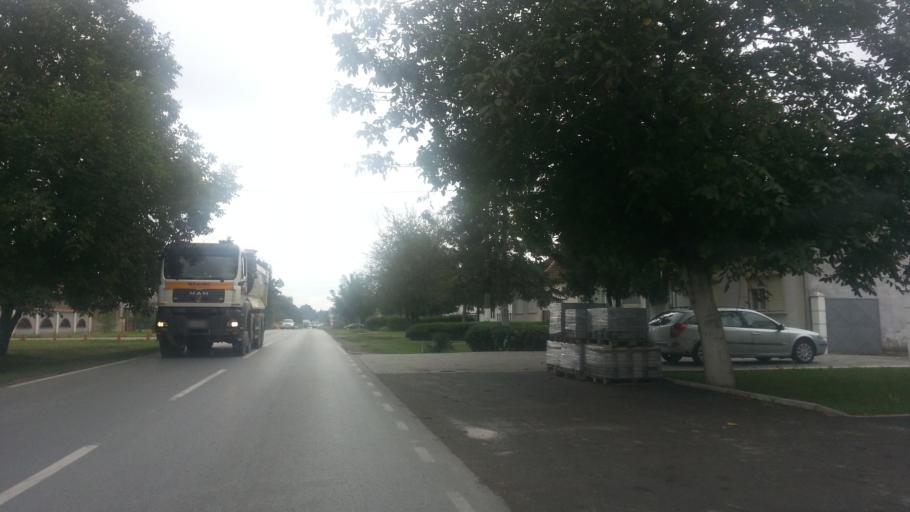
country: RS
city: Stari Banovci
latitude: 44.9792
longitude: 20.2809
